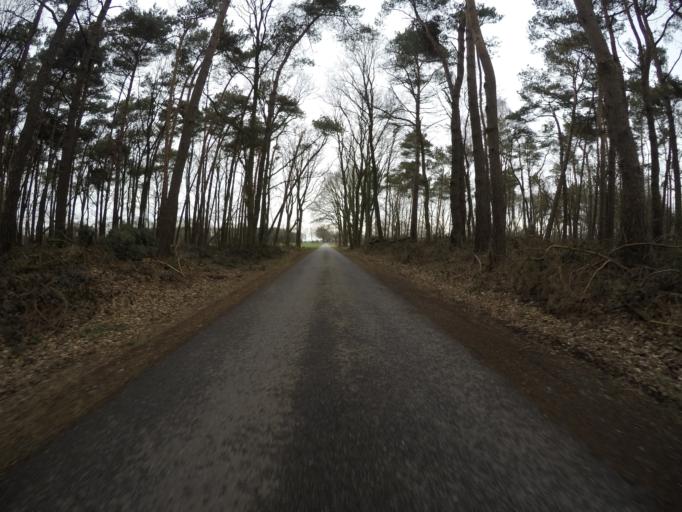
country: DE
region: North Rhine-Westphalia
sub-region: Regierungsbezirk Dusseldorf
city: Bocholt
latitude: 51.8035
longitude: 6.6290
